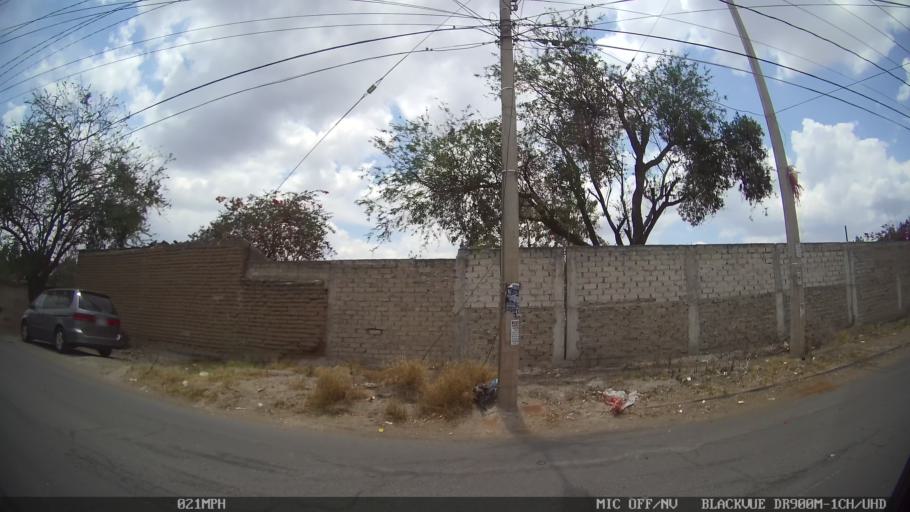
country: MX
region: Jalisco
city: Tonala
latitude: 20.6550
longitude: -103.2261
